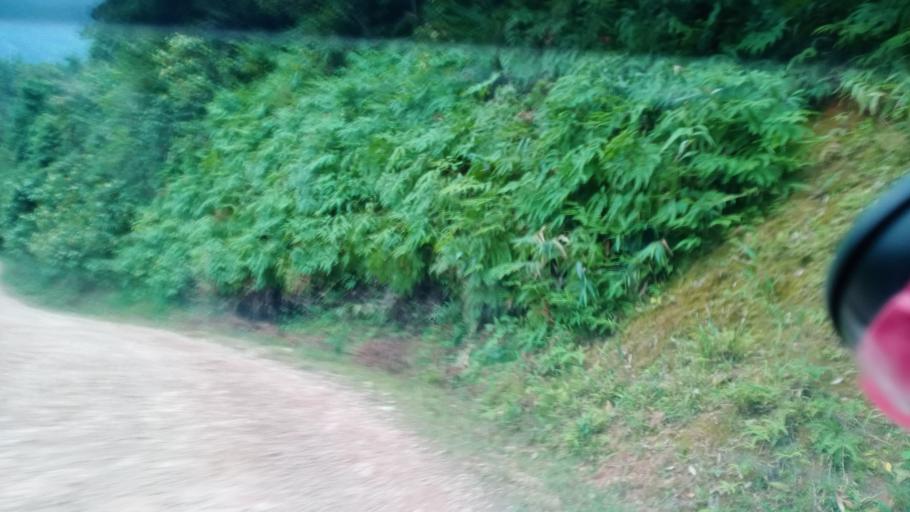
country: TH
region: Changwat Bueng Kan
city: Pak Khat
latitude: 18.7148
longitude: 103.2143
